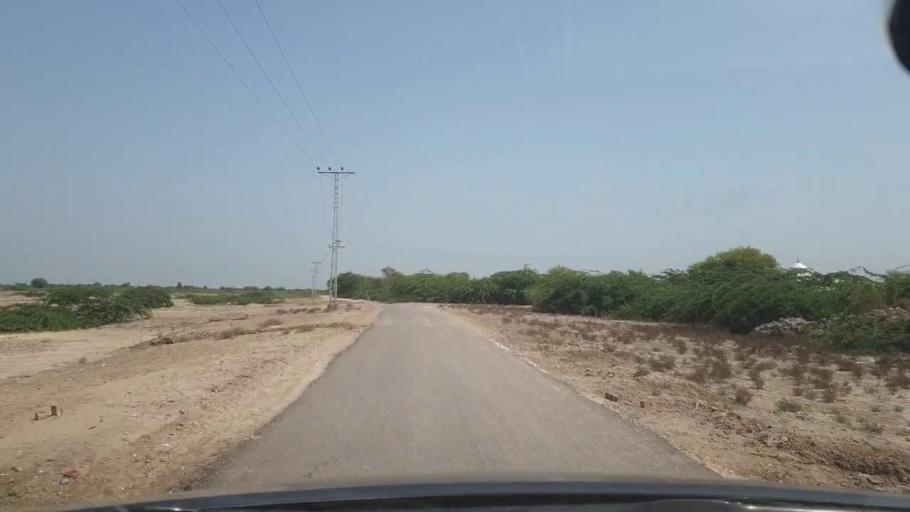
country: PK
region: Sindh
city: Naukot
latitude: 24.8135
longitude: 69.2203
